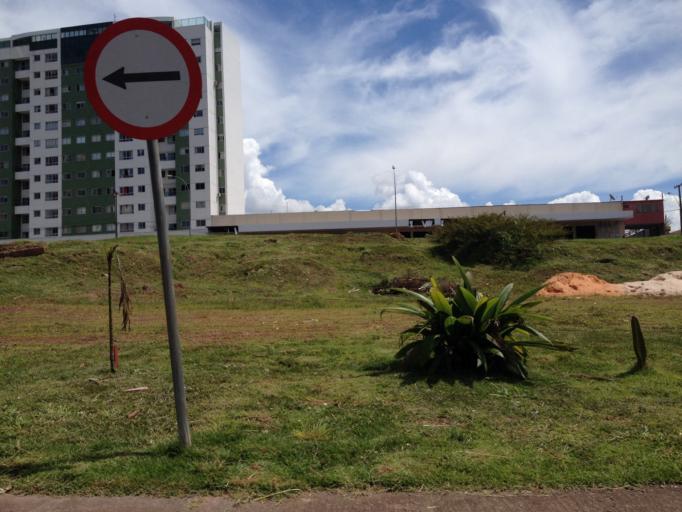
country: BR
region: Federal District
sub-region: Brasilia
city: Brasilia
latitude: -15.8297
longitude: -48.0313
